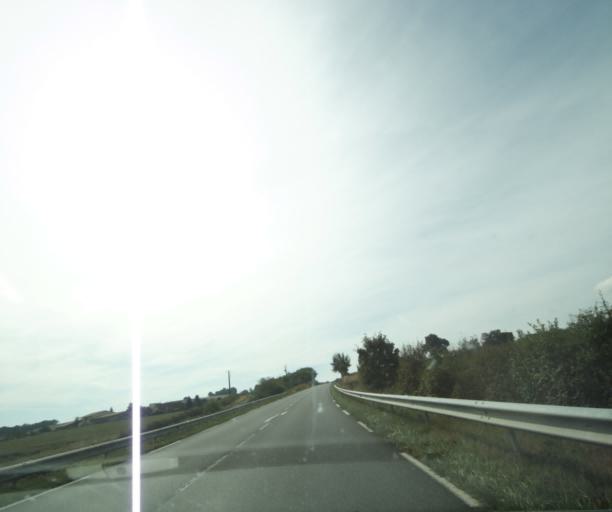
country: FR
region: Auvergne
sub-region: Departement de l'Allier
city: Le Donjon
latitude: 46.3169
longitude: 3.7702
